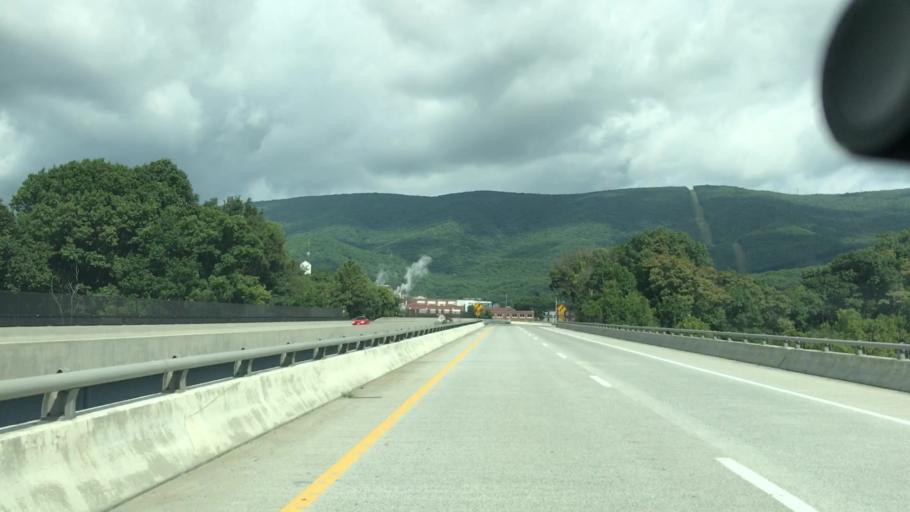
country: US
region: Virginia
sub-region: Giles County
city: Pearisburg
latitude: 37.3401
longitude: -80.7576
